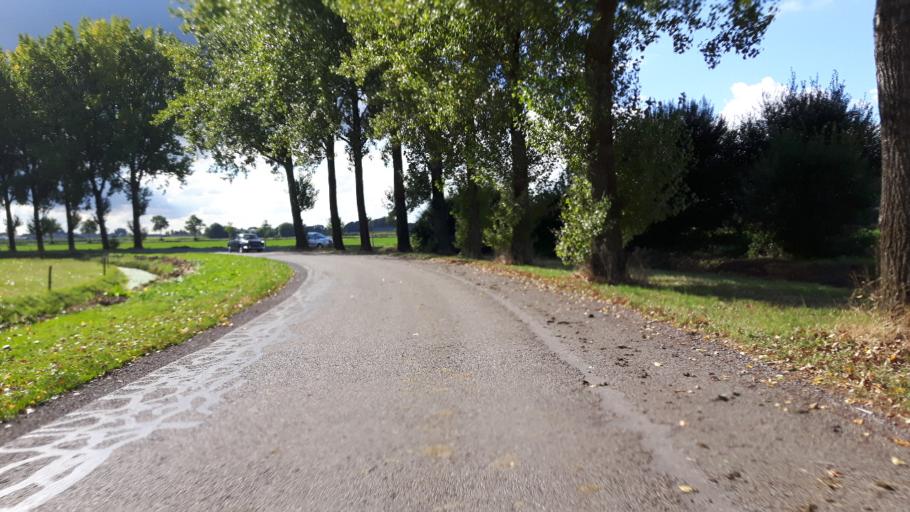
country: NL
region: South Holland
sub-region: Gemeente Leerdam
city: Leerdam
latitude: 51.8905
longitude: 5.1303
